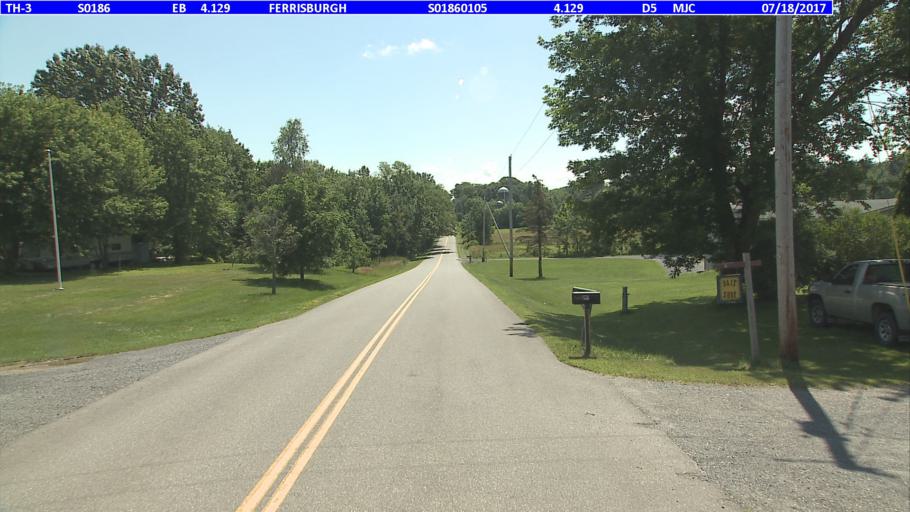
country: US
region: Vermont
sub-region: Addison County
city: Vergennes
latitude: 44.1693
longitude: -73.3001
